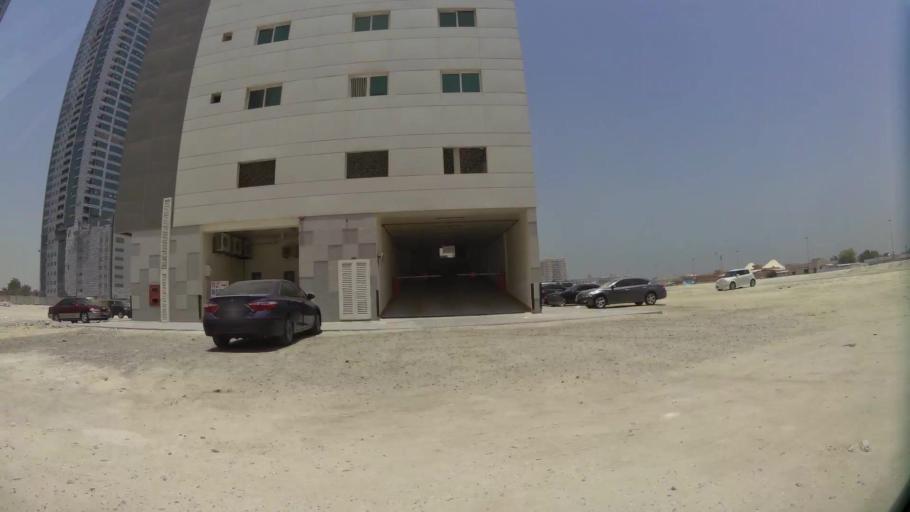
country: AE
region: Ash Shariqah
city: Sharjah
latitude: 25.3303
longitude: 55.3671
